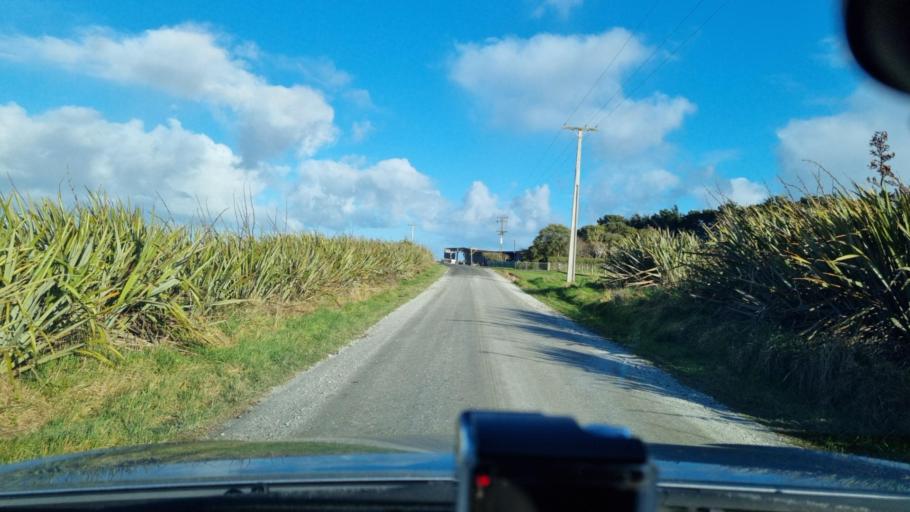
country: NZ
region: Southland
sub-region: Invercargill City
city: Bluff
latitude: -46.5244
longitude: 168.4101
